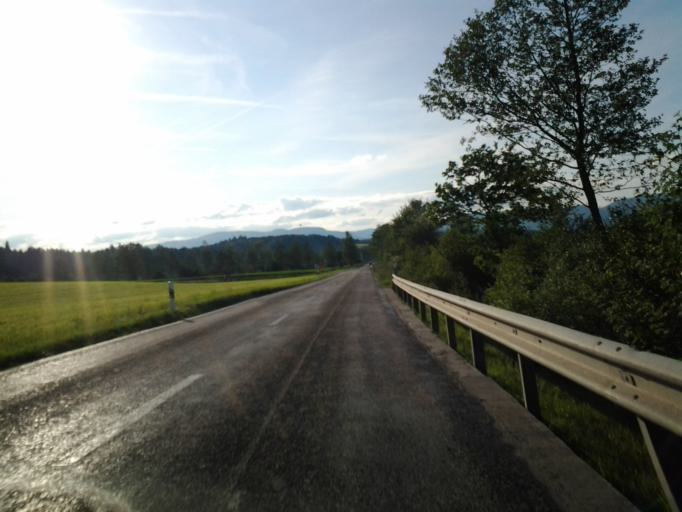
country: CH
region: Bern
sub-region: Oberaargau
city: Roggwil
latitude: 47.2218
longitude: 7.8511
